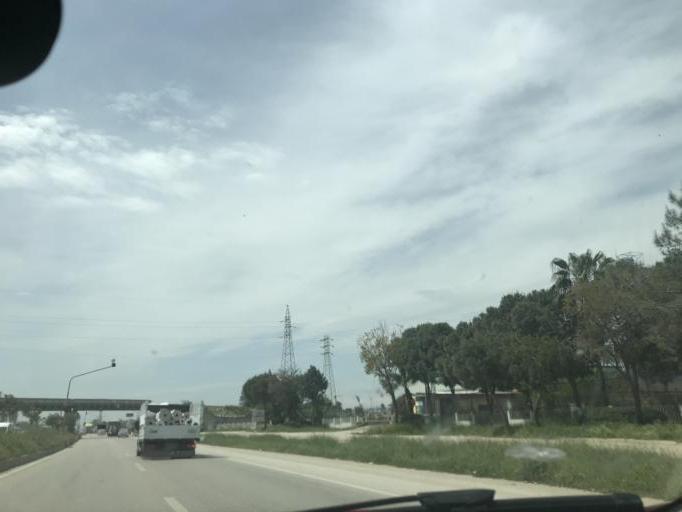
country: TR
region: Adana
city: Yuregir
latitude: 36.9812
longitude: 35.4431
